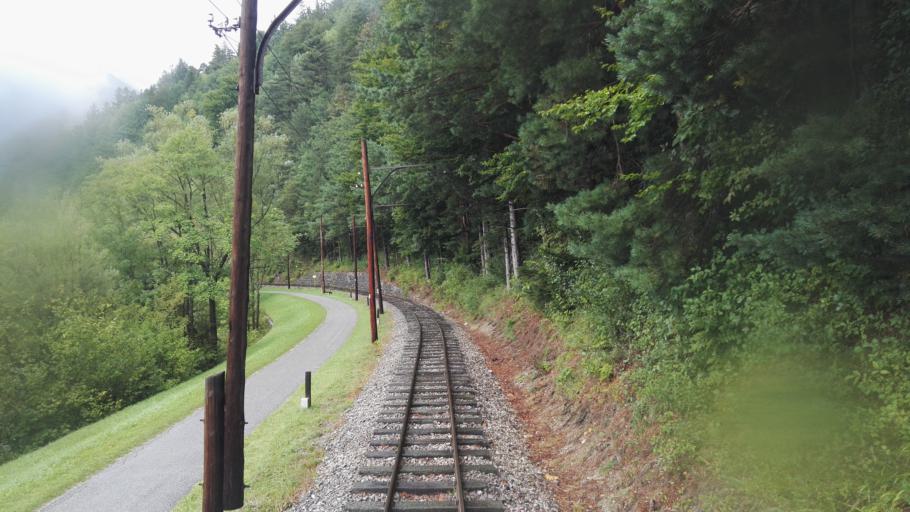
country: AT
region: Lower Austria
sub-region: Politischer Bezirk Neunkirchen
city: Reichenau an der Rax
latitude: 47.7060
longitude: 15.8220
